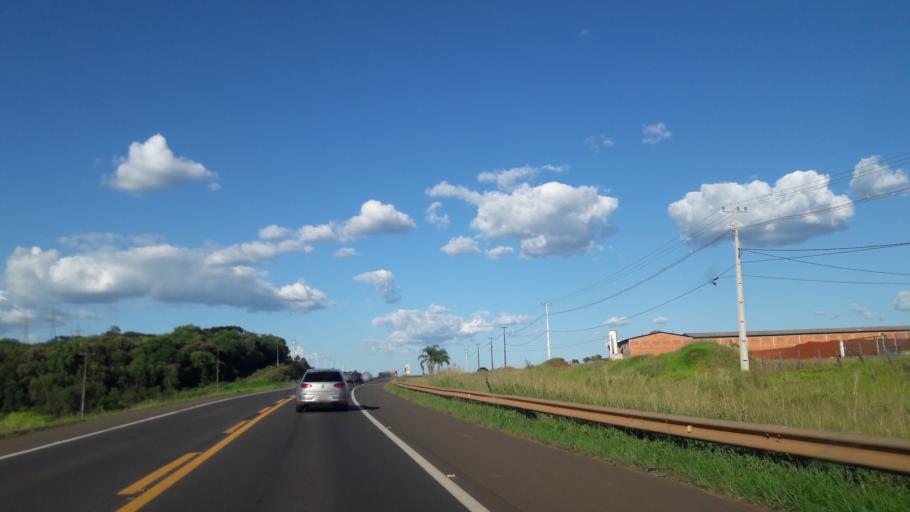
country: BR
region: Parana
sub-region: Guarapuava
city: Guarapuava
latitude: -25.3724
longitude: -51.5005
